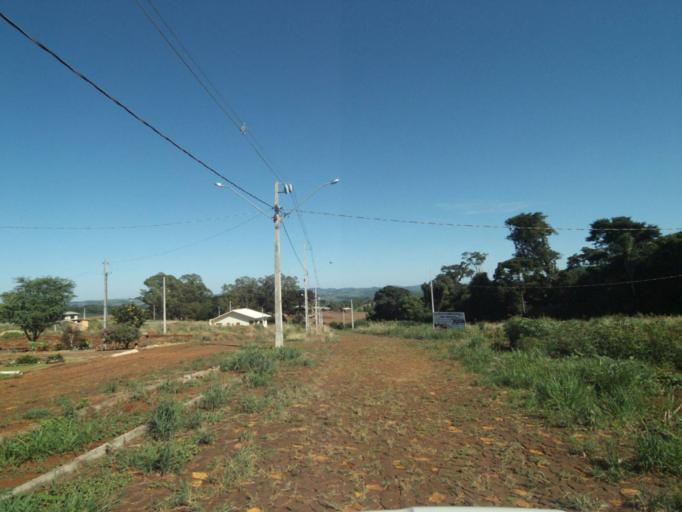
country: BR
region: Parana
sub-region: Laranjeiras Do Sul
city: Laranjeiras do Sul
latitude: -25.4856
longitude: -52.5255
